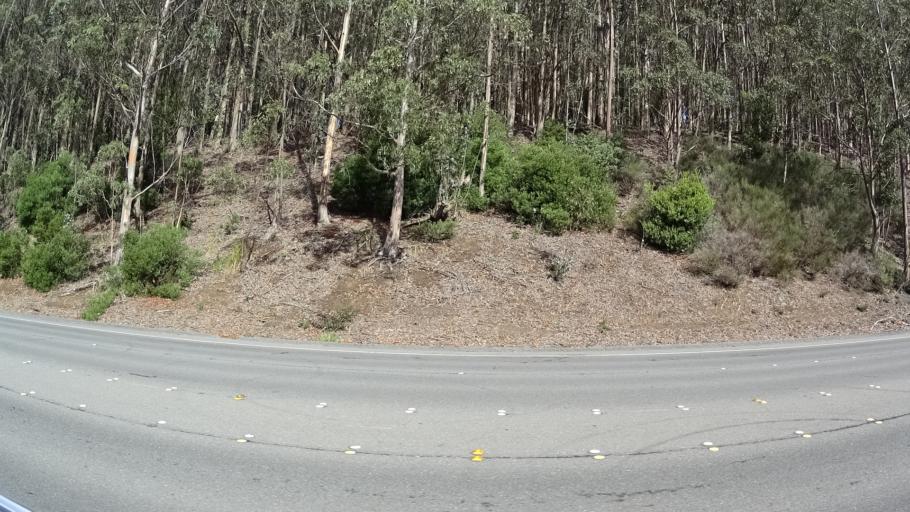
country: US
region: California
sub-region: San Mateo County
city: Daly City
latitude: 37.7000
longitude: -122.4436
